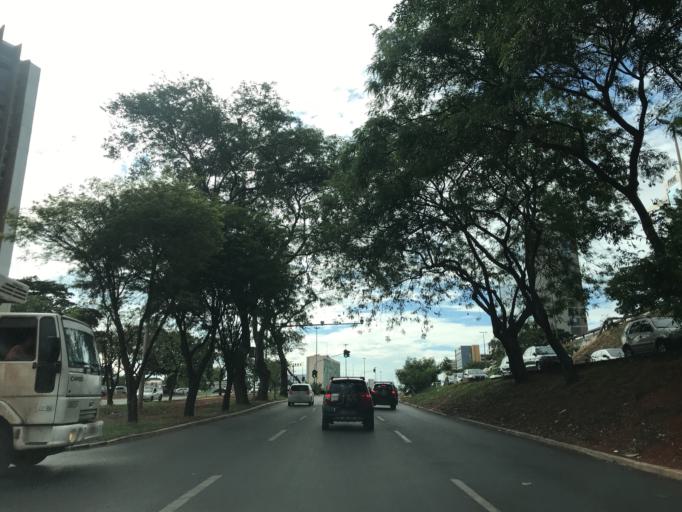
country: BR
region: Federal District
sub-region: Brasilia
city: Brasilia
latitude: -15.8022
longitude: -47.8822
